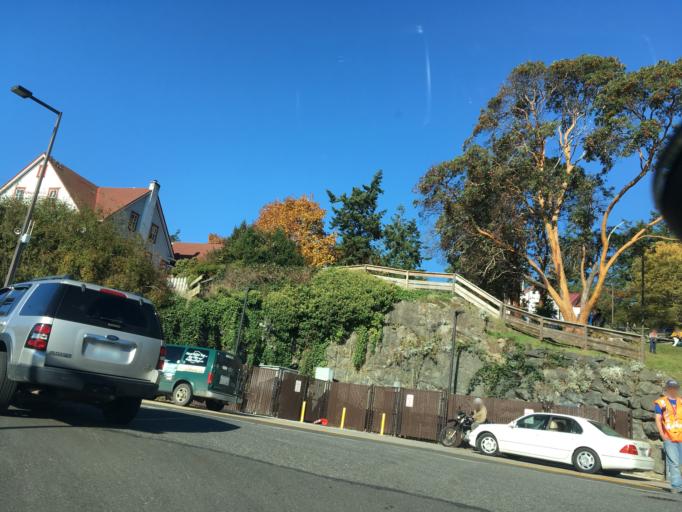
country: US
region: Washington
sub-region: San Juan County
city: Friday Harbor
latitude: 48.5977
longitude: -122.9441
